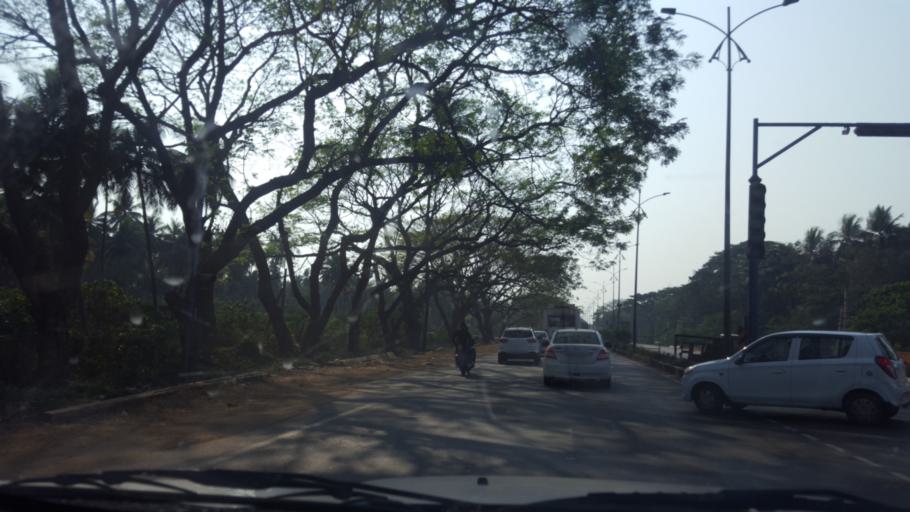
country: IN
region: Andhra Pradesh
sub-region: Vishakhapatnam
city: Anakapalle
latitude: 17.6759
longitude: 83.0138
